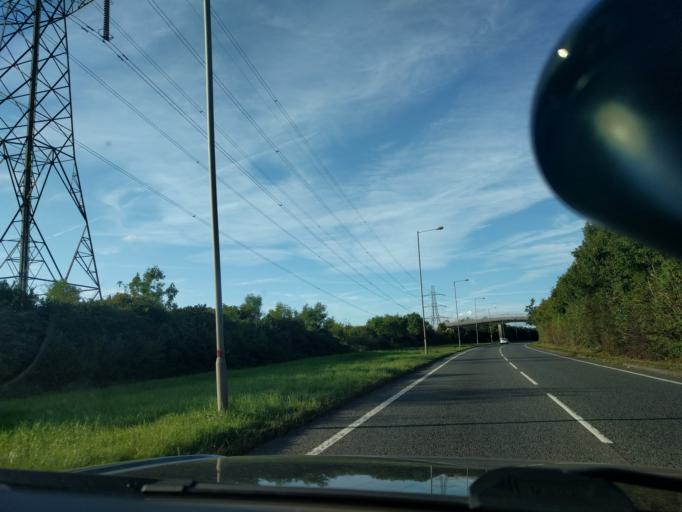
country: GB
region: England
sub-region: Wiltshire
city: Chippenham
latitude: 51.4612
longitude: -2.1505
